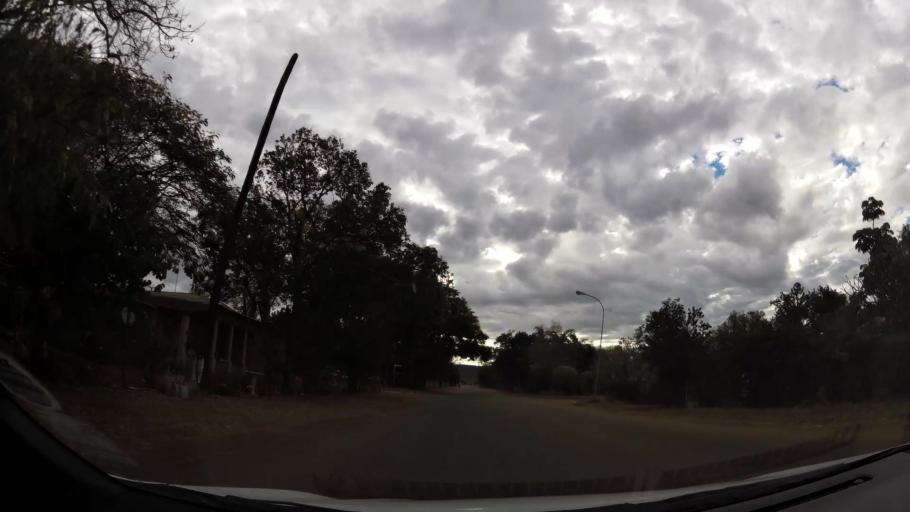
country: ZA
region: Limpopo
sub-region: Waterberg District Municipality
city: Modimolle
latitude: -24.5210
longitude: 28.7051
